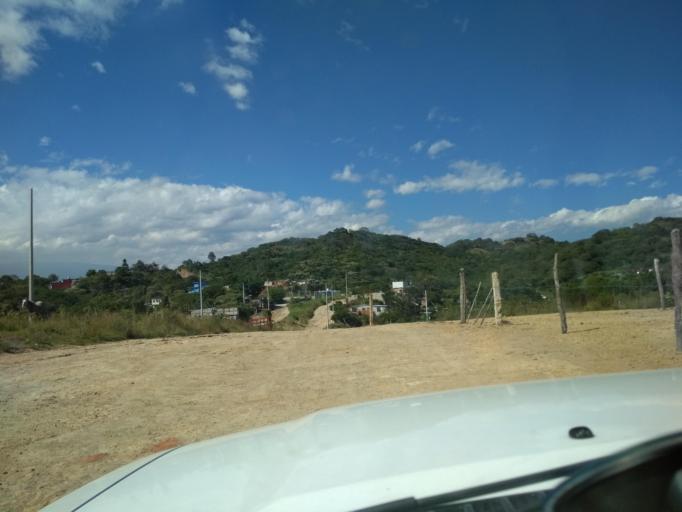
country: MX
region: Veracruz
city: El Castillo
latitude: 19.5488
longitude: -96.8564
